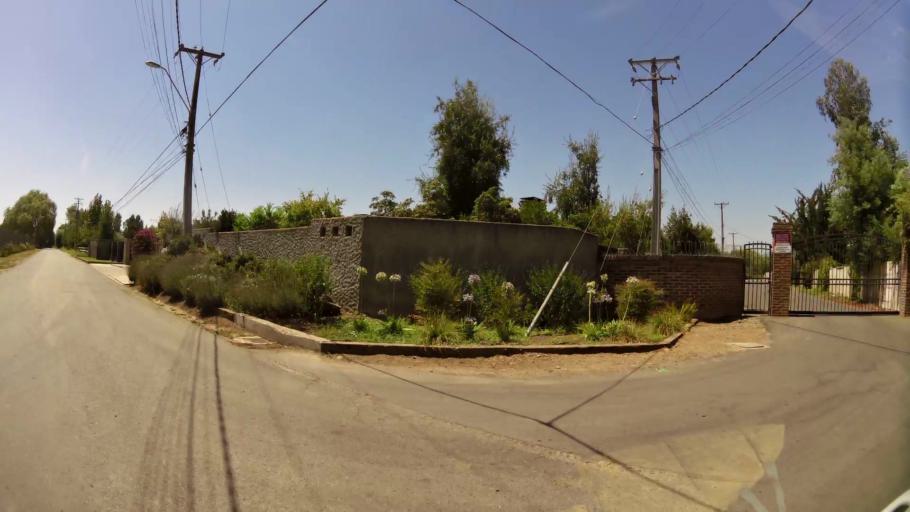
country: CL
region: Maule
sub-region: Provincia de Curico
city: Curico
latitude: -35.0011
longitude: -71.2099
